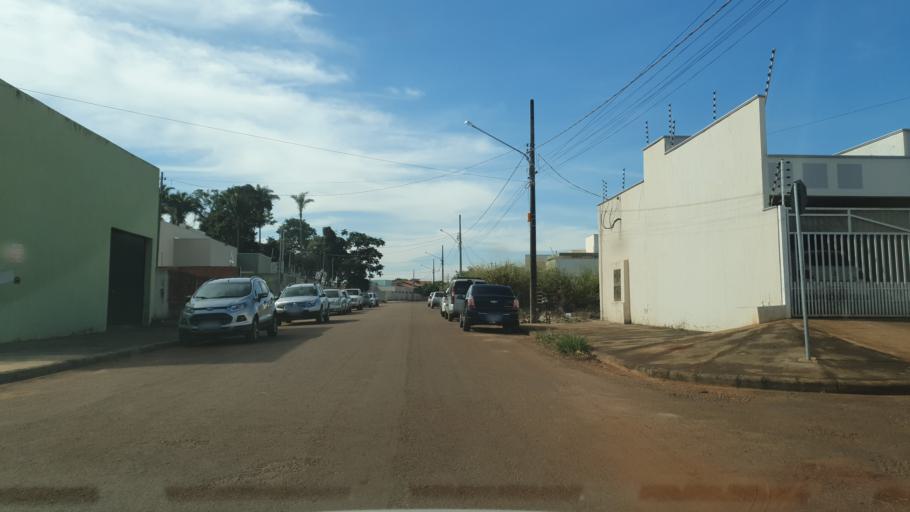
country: BR
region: Mato Grosso
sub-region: Pontes E Lacerda
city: Pontes e Lacerda
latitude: -15.2479
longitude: -59.3198
